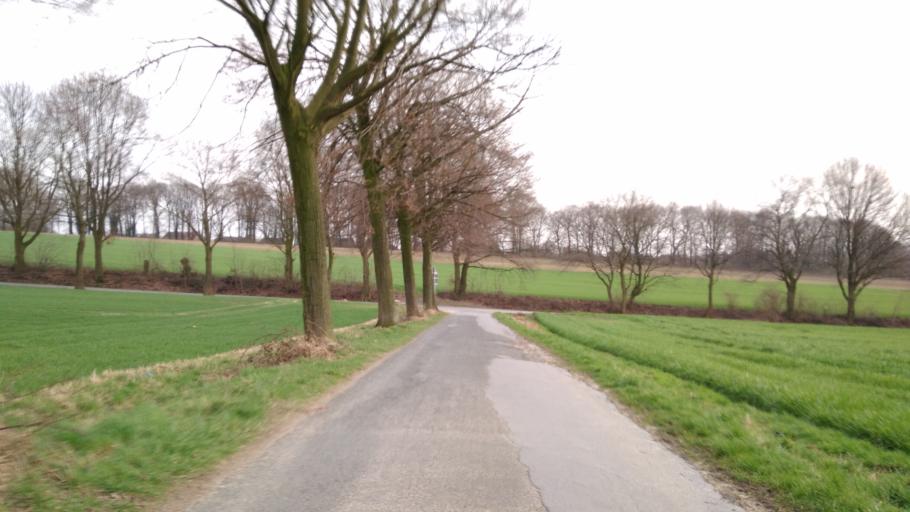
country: DE
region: North Rhine-Westphalia
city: Herten
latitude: 51.5993
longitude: 7.1209
